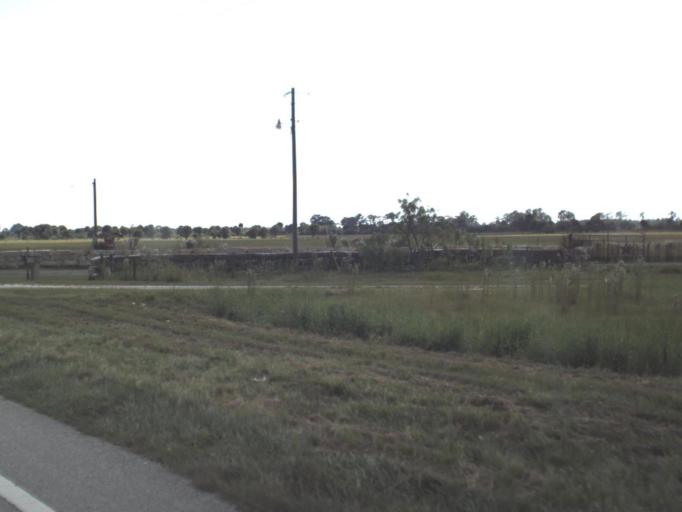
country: US
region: Florida
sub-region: Okeechobee County
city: Okeechobee
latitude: 27.2879
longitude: -80.8841
